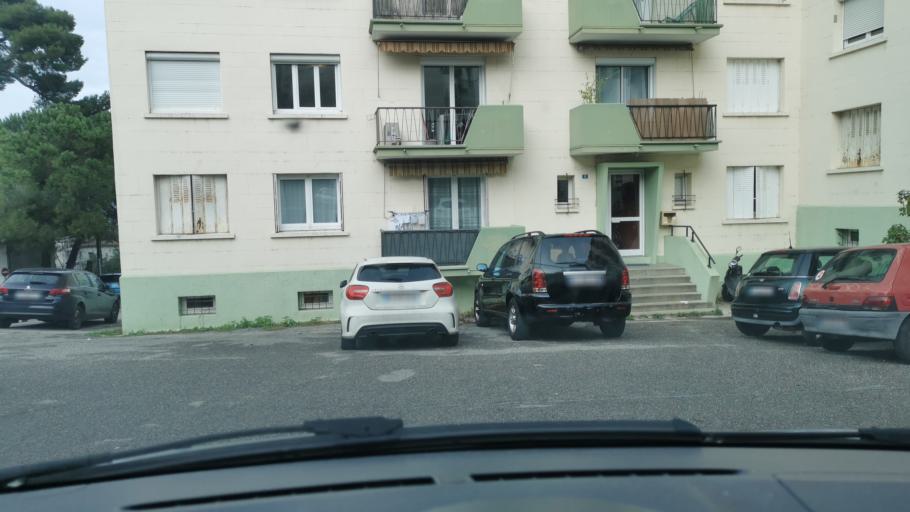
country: FR
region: Languedoc-Roussillon
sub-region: Departement de l'Herault
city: Sete
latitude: 43.4083
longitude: 3.6775
